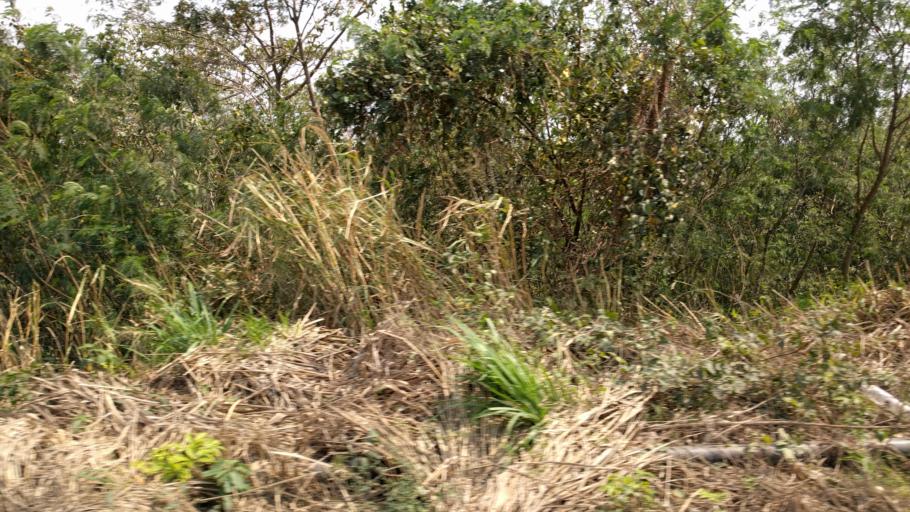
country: BO
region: Santa Cruz
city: Santa Rita
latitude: -17.9199
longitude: -63.3462
